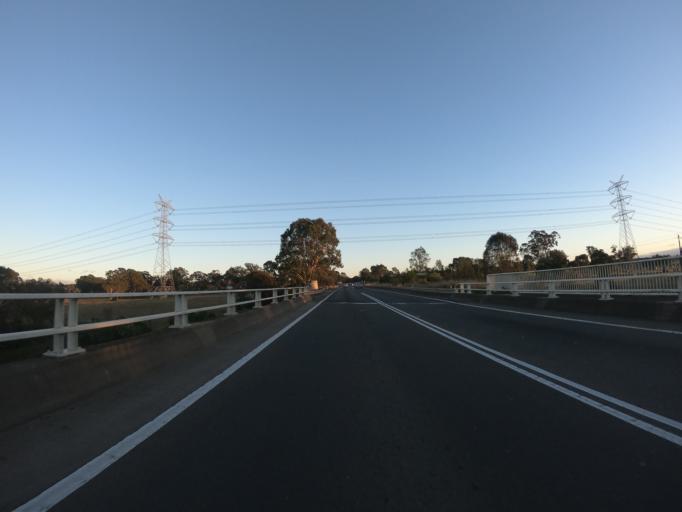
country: AU
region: New South Wales
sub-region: Blacktown
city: Riverstone
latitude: -33.6774
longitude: 150.8121
